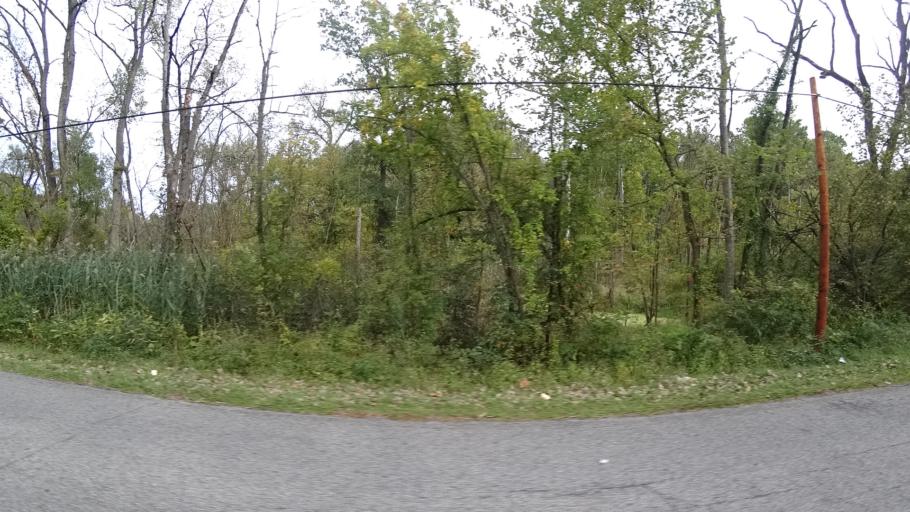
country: US
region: Indiana
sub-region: LaPorte County
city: Trail Creek
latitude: 41.6943
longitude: -86.8163
